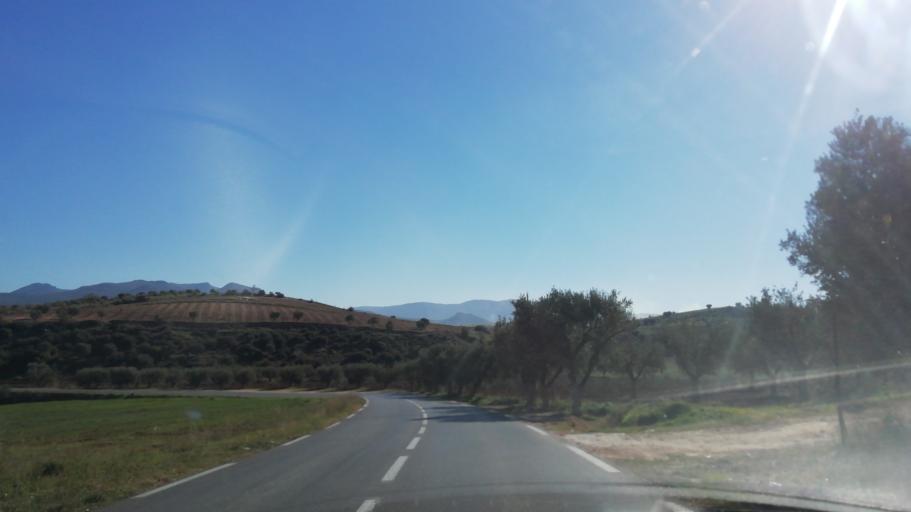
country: DZ
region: Tlemcen
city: Beni Mester
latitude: 34.8269
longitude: -1.5776
